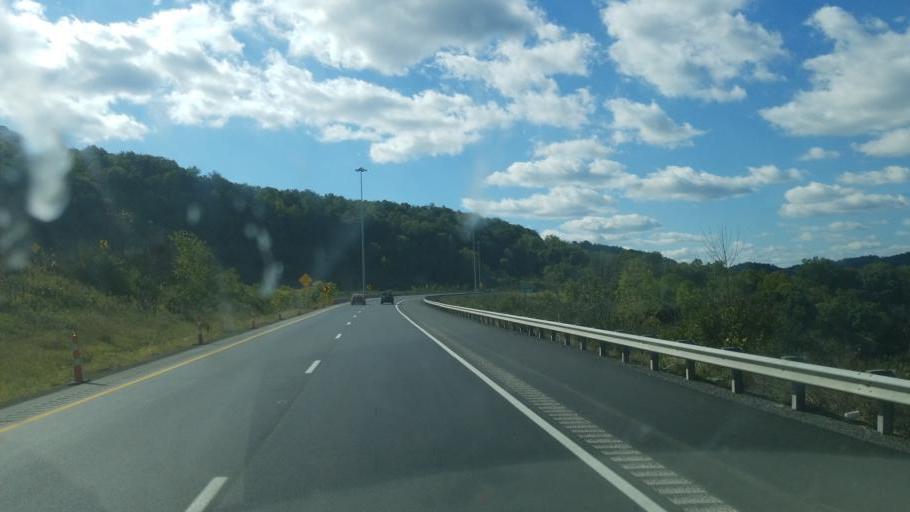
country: US
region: West Virginia
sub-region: Monongalia County
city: Morgantown
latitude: 39.5798
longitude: -79.9731
